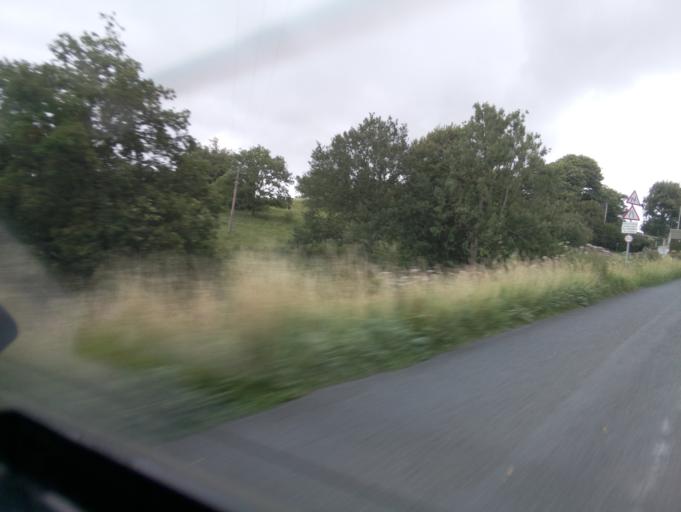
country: GB
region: England
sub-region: Gloucestershire
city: Shurdington
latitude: 51.8148
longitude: -2.1480
